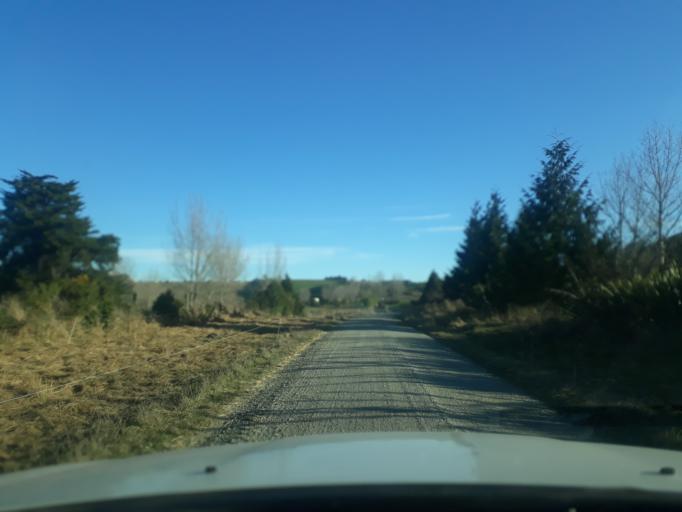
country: NZ
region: Canterbury
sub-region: Timaru District
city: Pleasant Point
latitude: -44.3415
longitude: 171.1636
